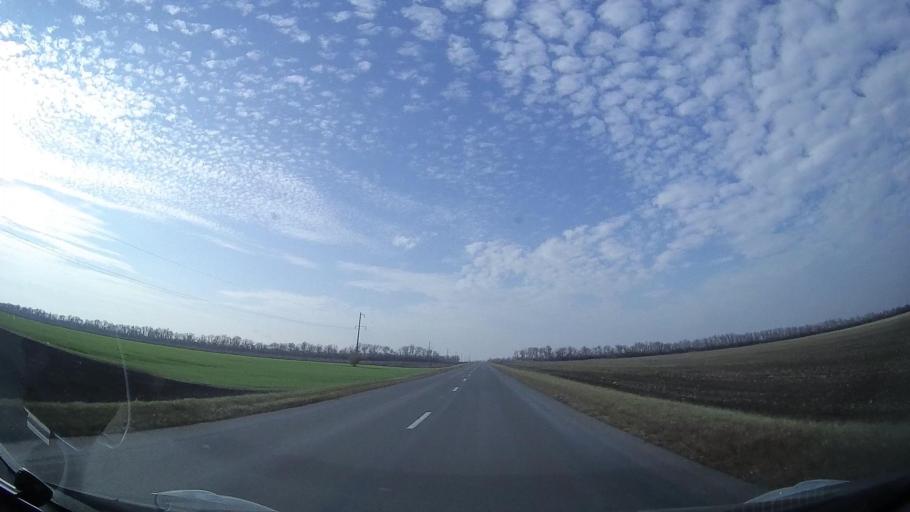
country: RU
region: Rostov
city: Veselyy
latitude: 46.9694
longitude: 40.6697
